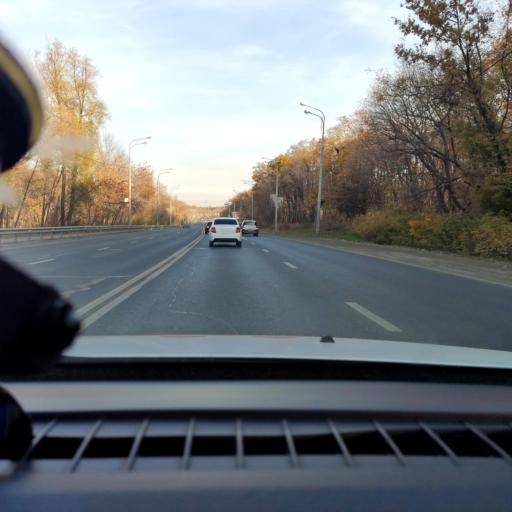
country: RU
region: Samara
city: Samara
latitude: 53.2828
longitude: 50.2283
